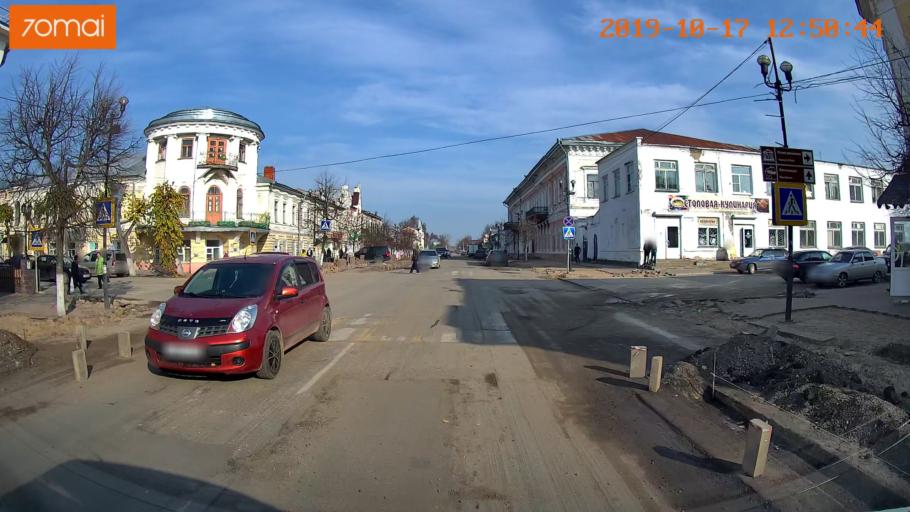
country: RU
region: Rjazan
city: Kasimov
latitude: 54.9389
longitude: 41.3946
